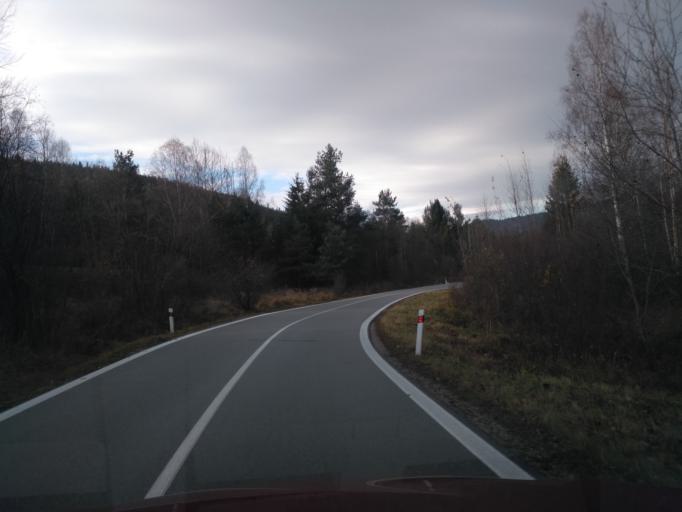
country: SK
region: Kosicky
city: Spisska Nova Ves
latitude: 48.8191
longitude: 20.6604
